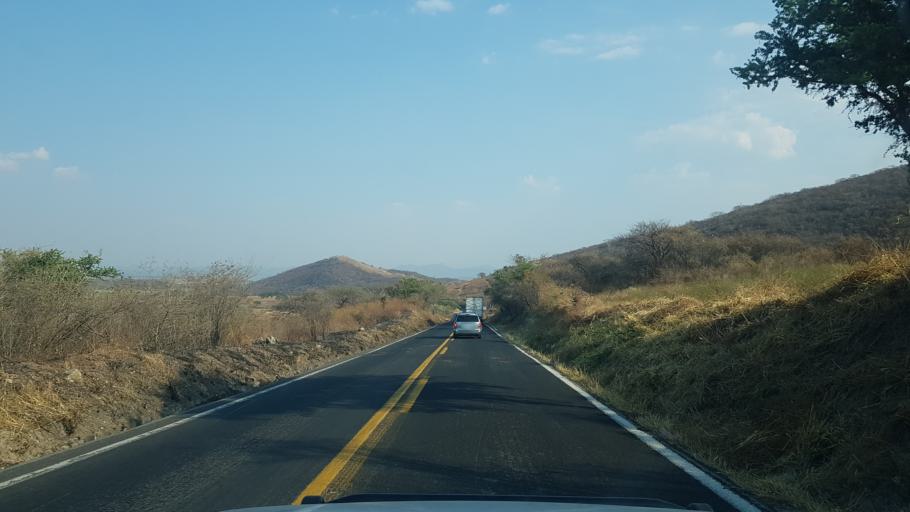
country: MX
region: Puebla
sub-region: Tilapa
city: San Felix Rijo
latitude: 18.6387
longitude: -98.5873
